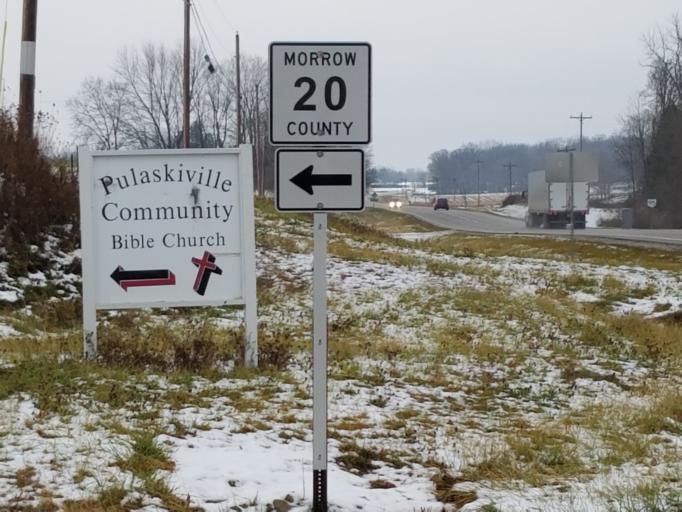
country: US
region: Ohio
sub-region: Morrow County
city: Mount Gilead
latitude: 40.5142
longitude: -82.7425
